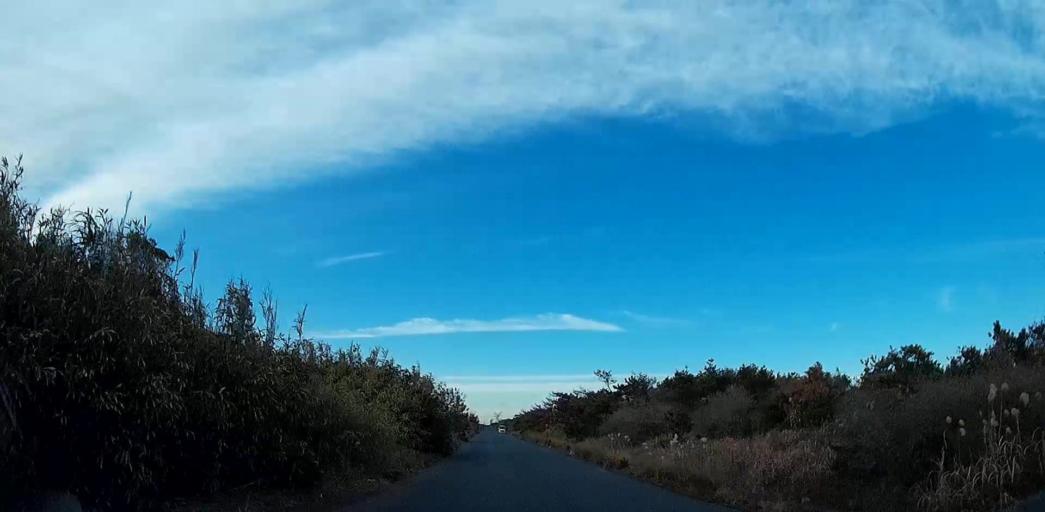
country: JP
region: Chiba
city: Hasaki
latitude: 35.7961
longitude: 140.7935
